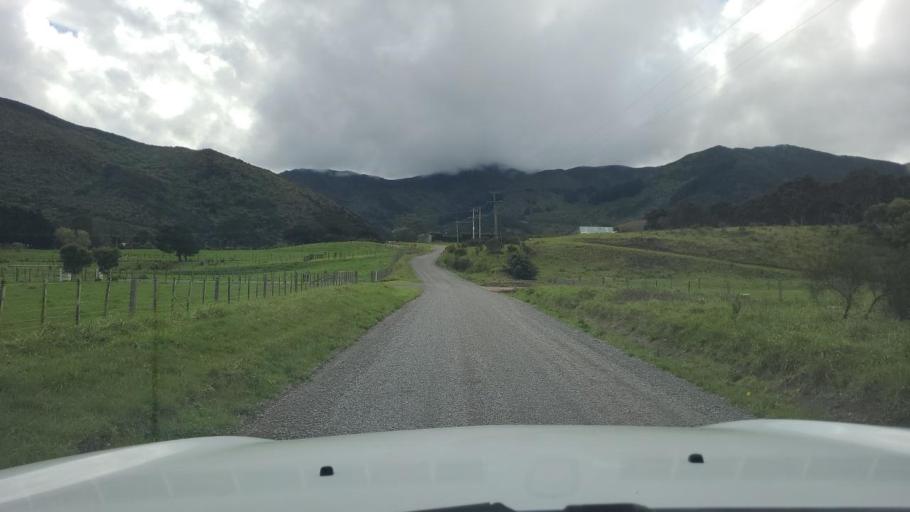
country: NZ
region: Wellington
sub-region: Upper Hutt City
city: Upper Hutt
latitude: -41.1707
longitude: 175.2441
